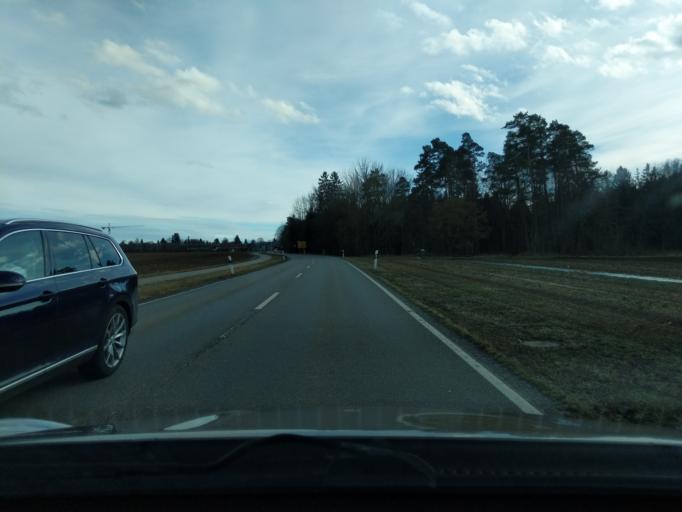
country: DE
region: Bavaria
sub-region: Upper Bavaria
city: Vaterstetten
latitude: 48.1199
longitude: 11.7674
